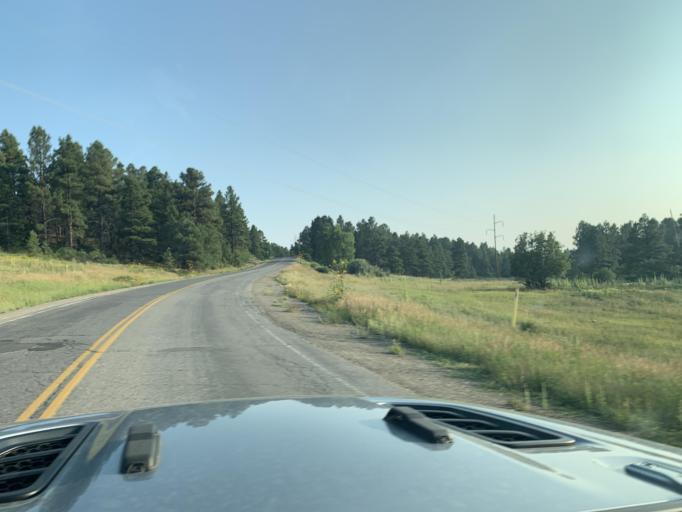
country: US
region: Colorado
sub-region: Archuleta County
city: Pagosa Springs
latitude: 37.2837
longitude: -107.0952
